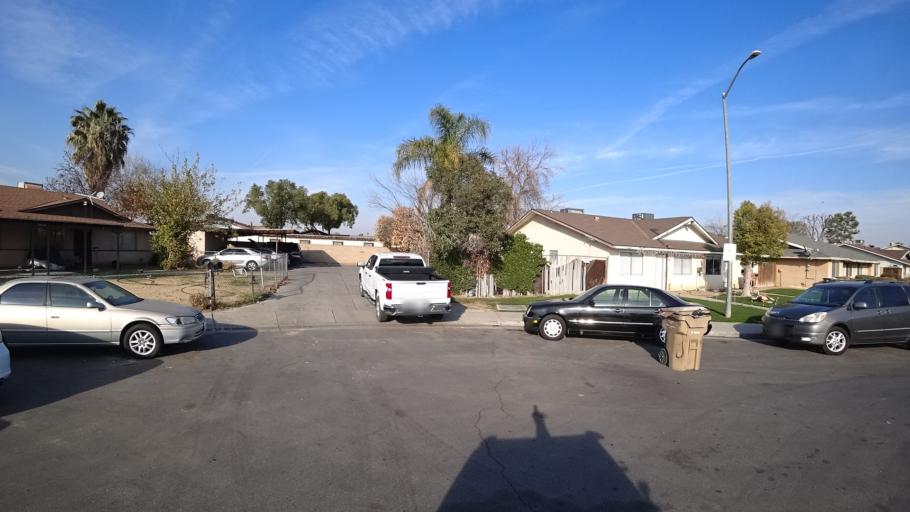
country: US
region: California
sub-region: Kern County
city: Bakersfield
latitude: 35.3203
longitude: -119.0311
